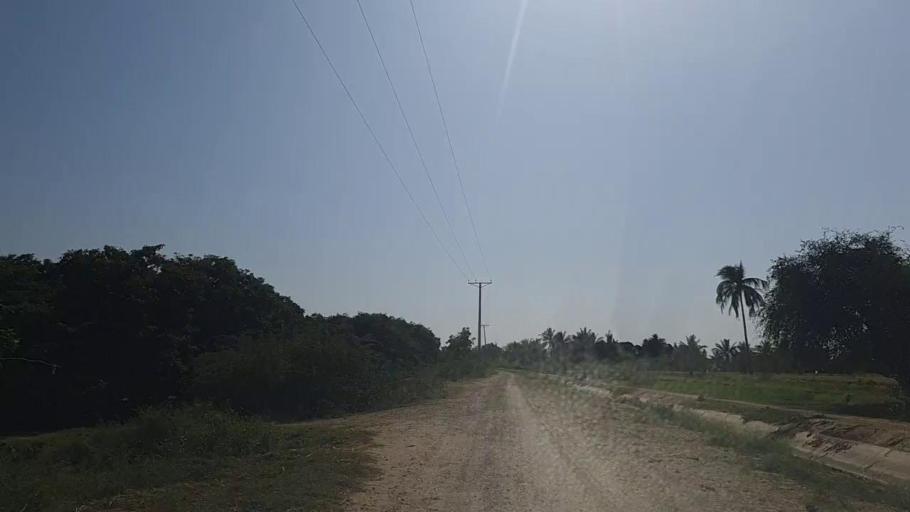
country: PK
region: Sindh
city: Thatta
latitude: 24.6299
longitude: 67.8784
